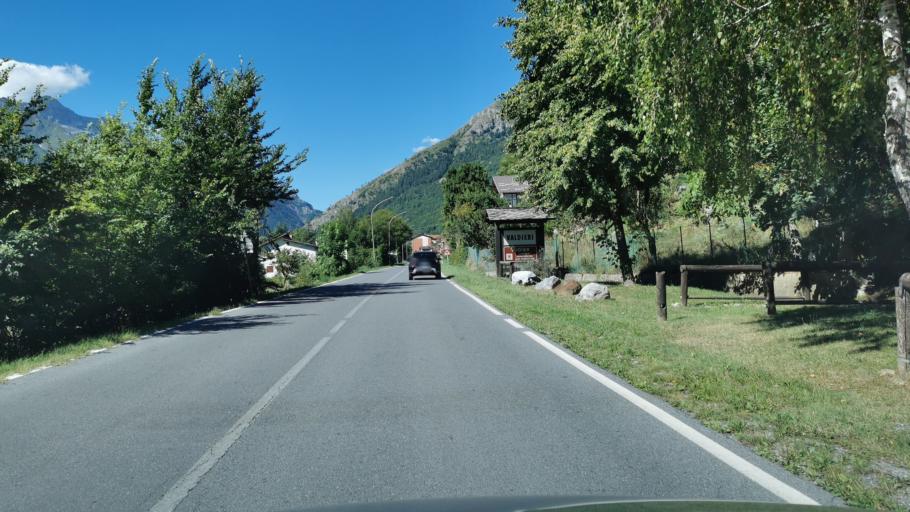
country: IT
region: Piedmont
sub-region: Provincia di Cuneo
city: Valdieri
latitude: 44.2799
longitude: 7.4056
